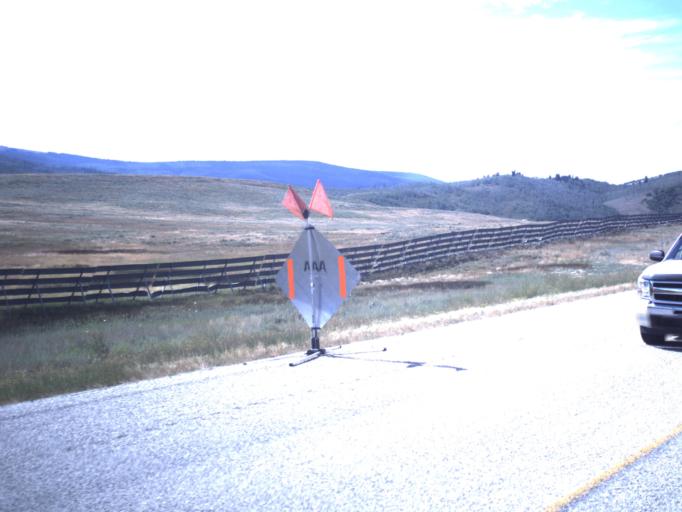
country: US
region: Utah
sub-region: Wasatch County
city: Heber
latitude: 40.2742
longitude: -111.2139
